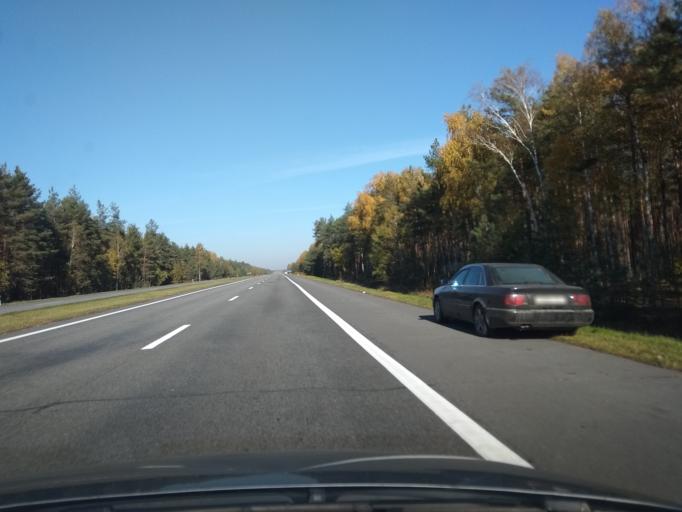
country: BY
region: Grodnenskaya
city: Zhyrovichy
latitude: 52.8919
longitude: 25.6702
